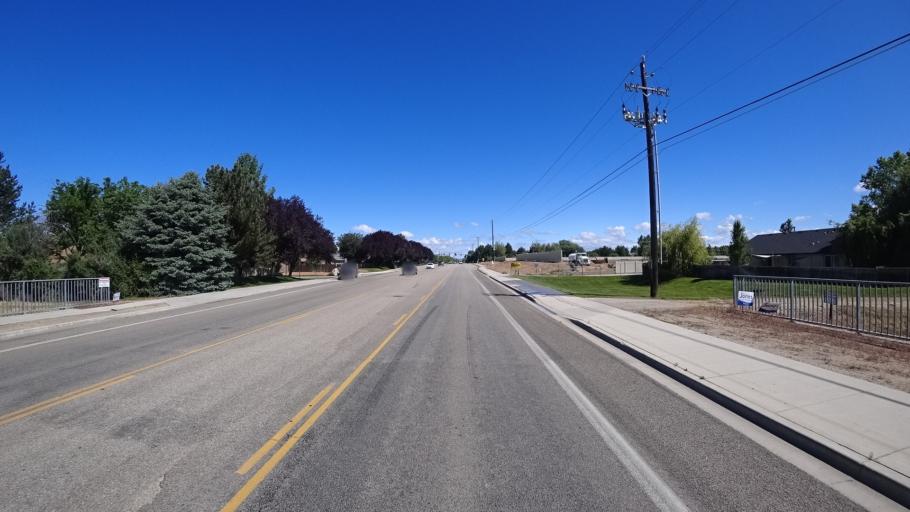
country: US
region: Idaho
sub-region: Ada County
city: Meridian
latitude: 43.6316
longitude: -116.3745
